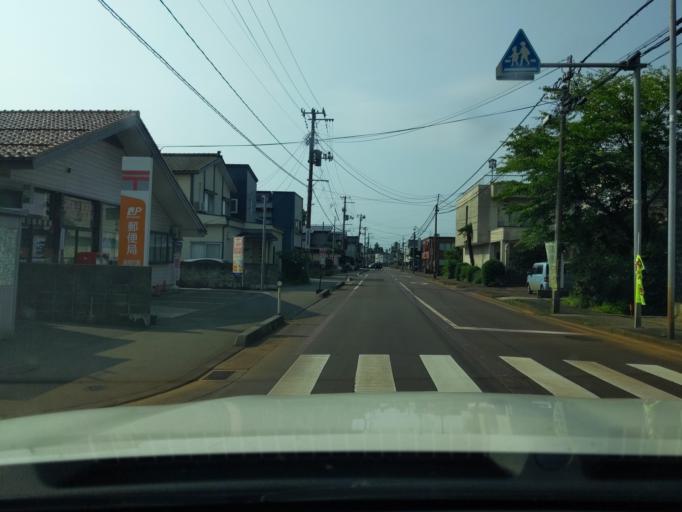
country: JP
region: Niigata
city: Nagaoka
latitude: 37.4324
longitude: 138.8592
